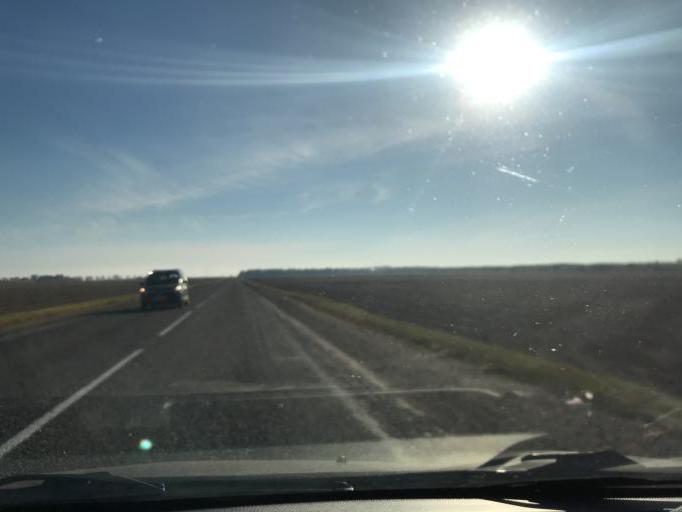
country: BY
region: Gomel
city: Brahin
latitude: 51.7880
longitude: 30.1910
